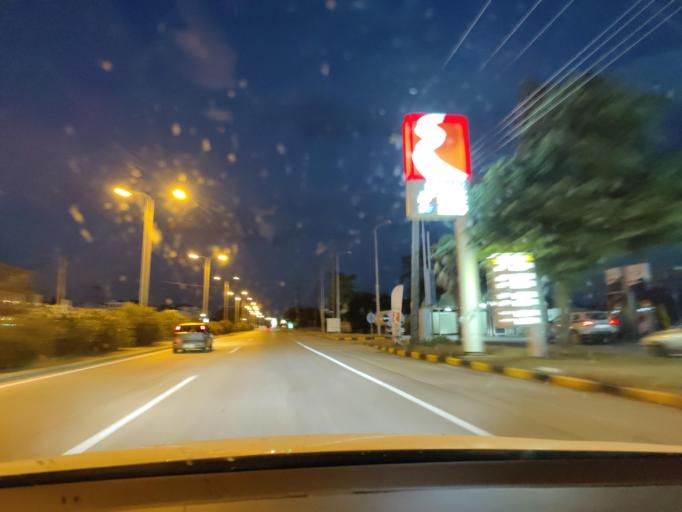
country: GR
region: Central Macedonia
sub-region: Nomos Serron
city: Lefkonas
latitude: 41.0902
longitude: 23.5179
